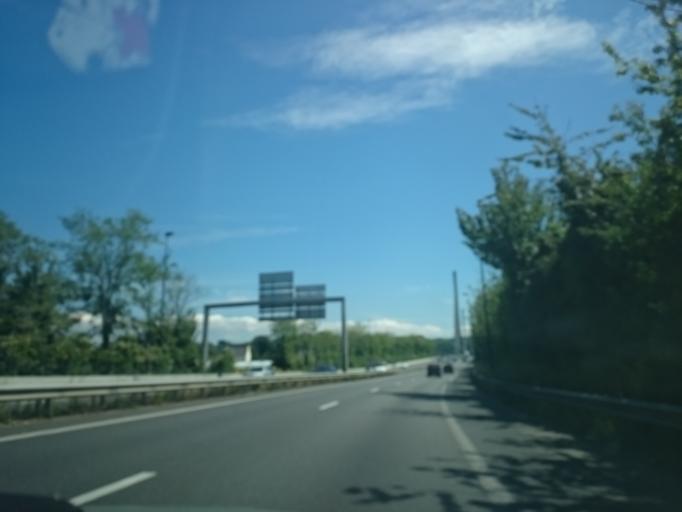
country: FR
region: Brittany
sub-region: Departement du Finistere
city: Le Relecq-Kerhuon
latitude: 48.3934
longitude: -4.4047
